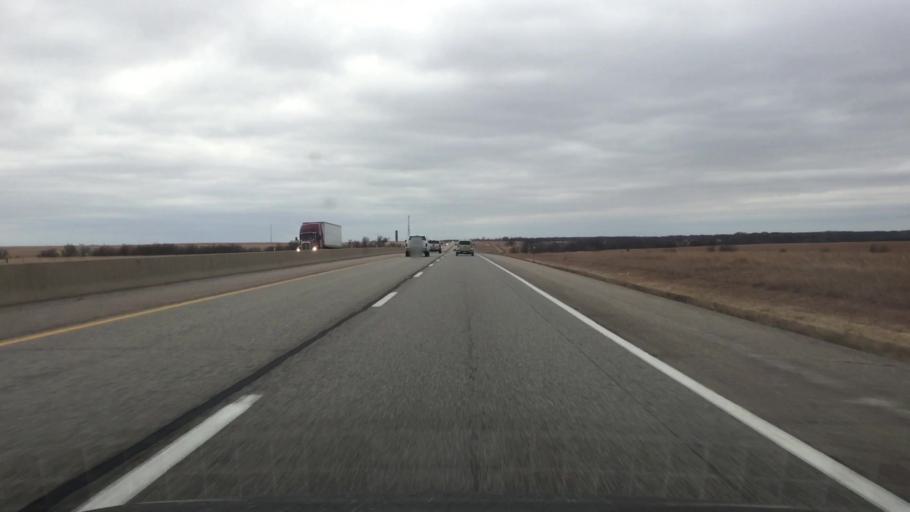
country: US
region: Kansas
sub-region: Butler County
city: El Dorado
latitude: 37.9763
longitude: -96.7162
